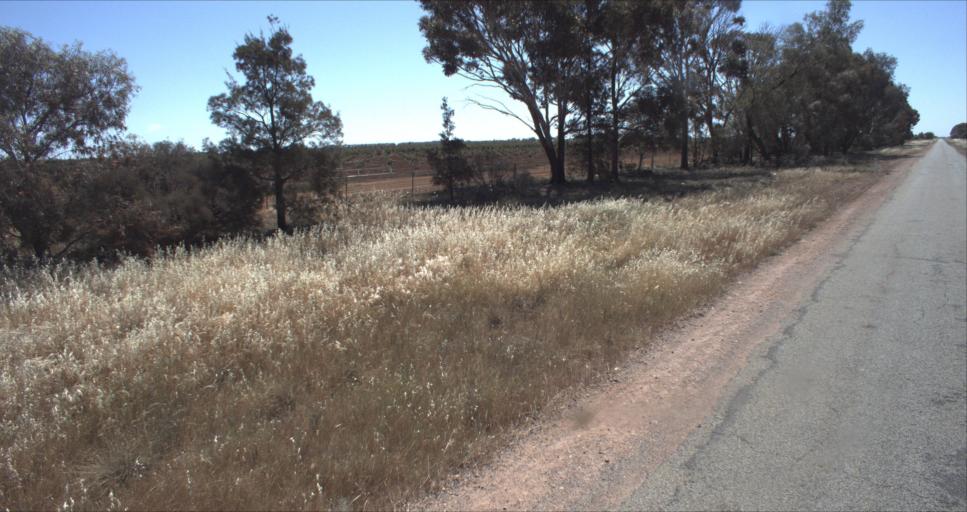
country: AU
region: New South Wales
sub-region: Leeton
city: Leeton
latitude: -34.5193
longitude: 146.3455
